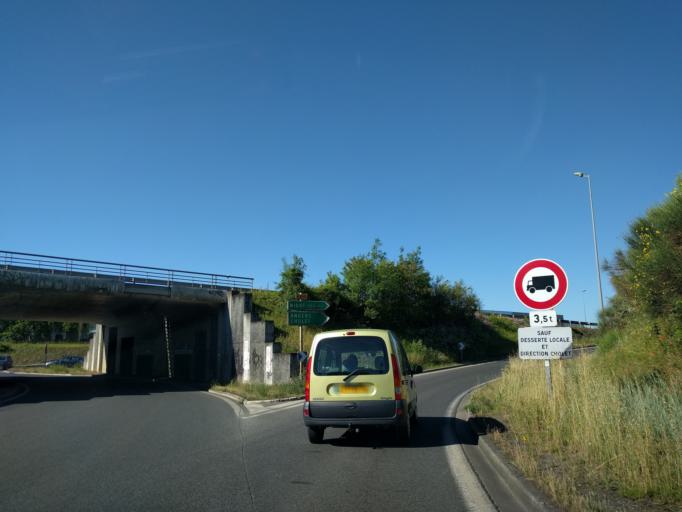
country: FR
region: Poitou-Charentes
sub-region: Departement des Deux-Sevres
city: Chauray
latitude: 46.3395
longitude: -0.4092
